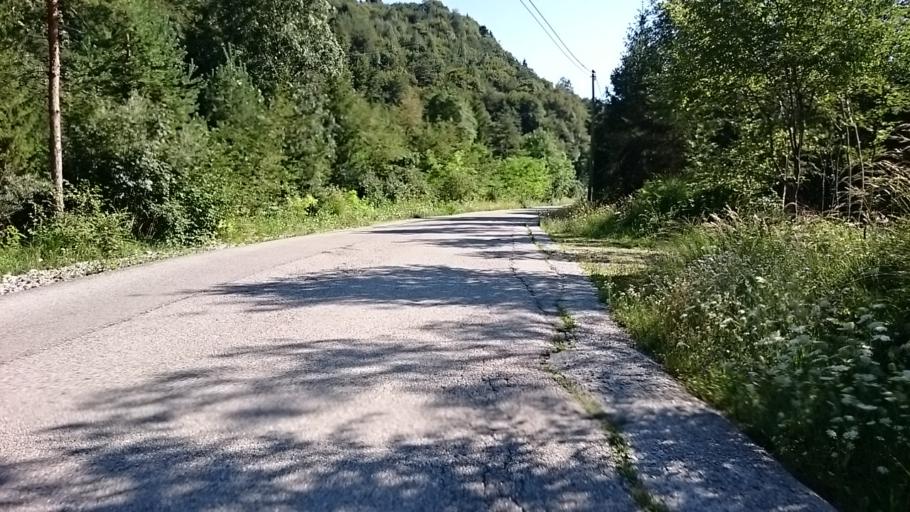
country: IT
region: Veneto
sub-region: Provincia di Belluno
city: Longarone
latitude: 46.2370
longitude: 12.3072
